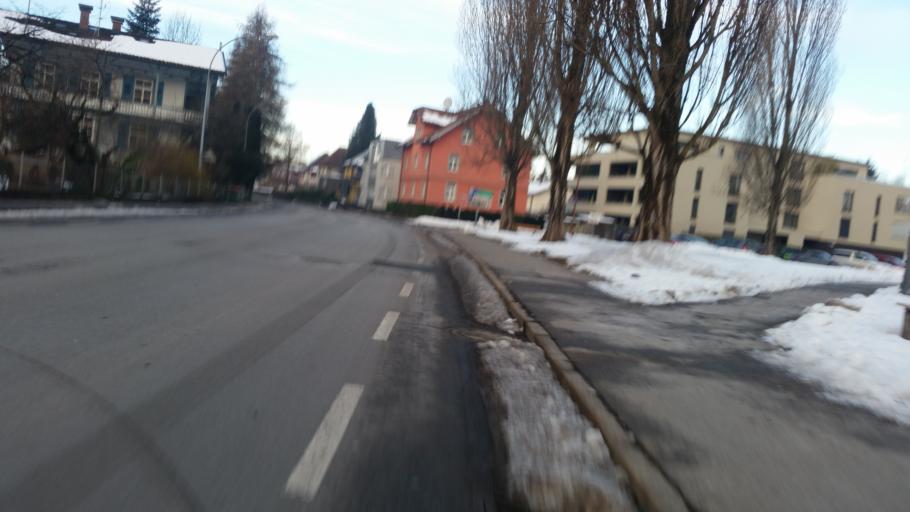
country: AT
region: Vorarlberg
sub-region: Politischer Bezirk Bregenz
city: Bregenz
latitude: 47.5030
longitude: 9.7330
